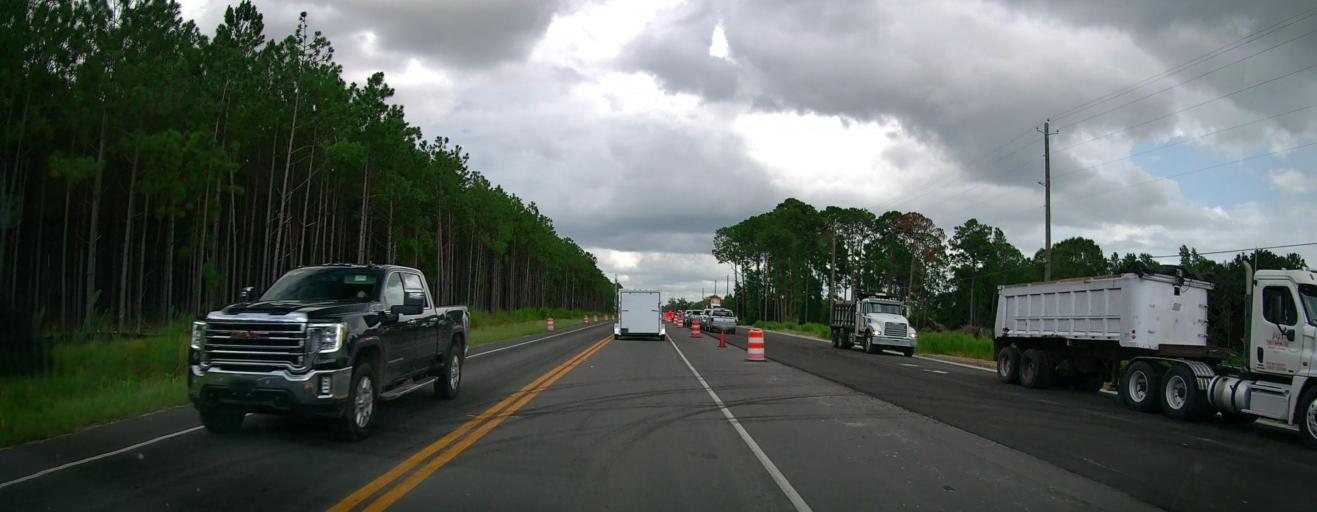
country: US
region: Georgia
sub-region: Coffee County
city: Douglas
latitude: 31.5207
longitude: -82.8912
